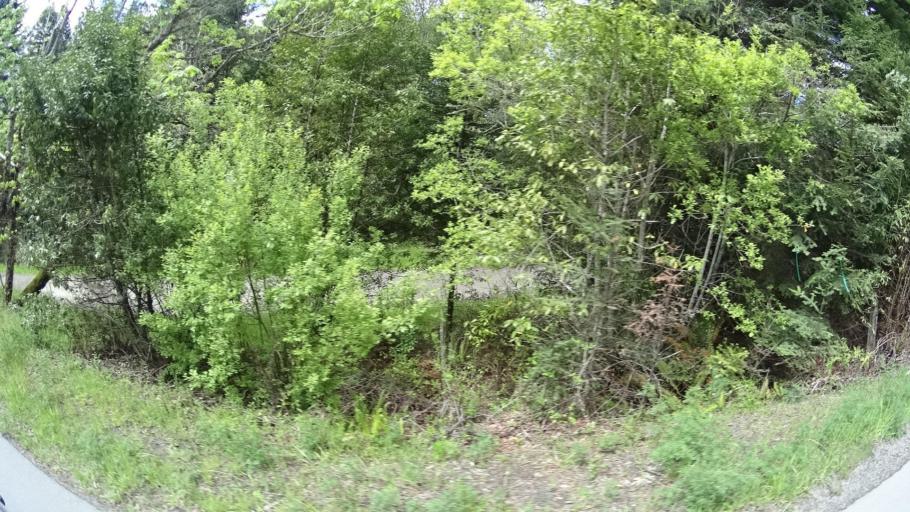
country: US
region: California
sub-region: Humboldt County
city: Blue Lake
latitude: 40.9035
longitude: -123.9865
